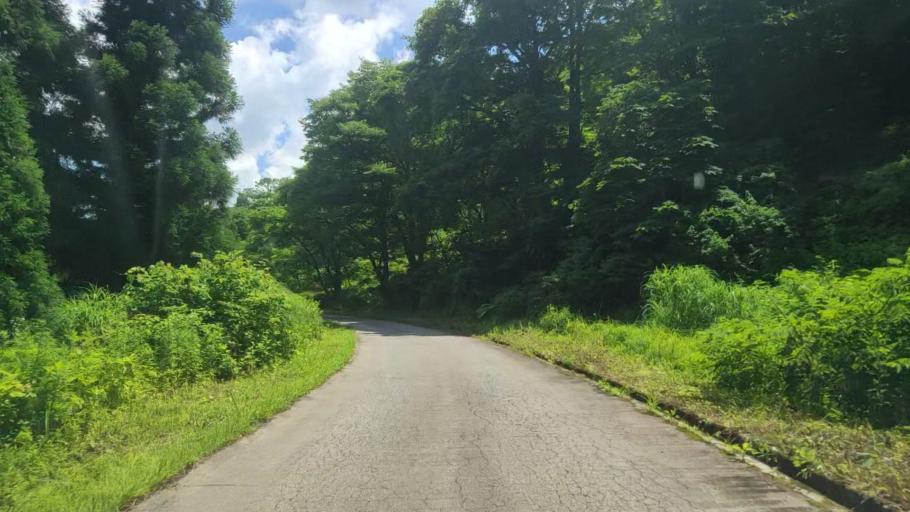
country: JP
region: Fukui
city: Ono
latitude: 35.8234
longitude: 136.4472
